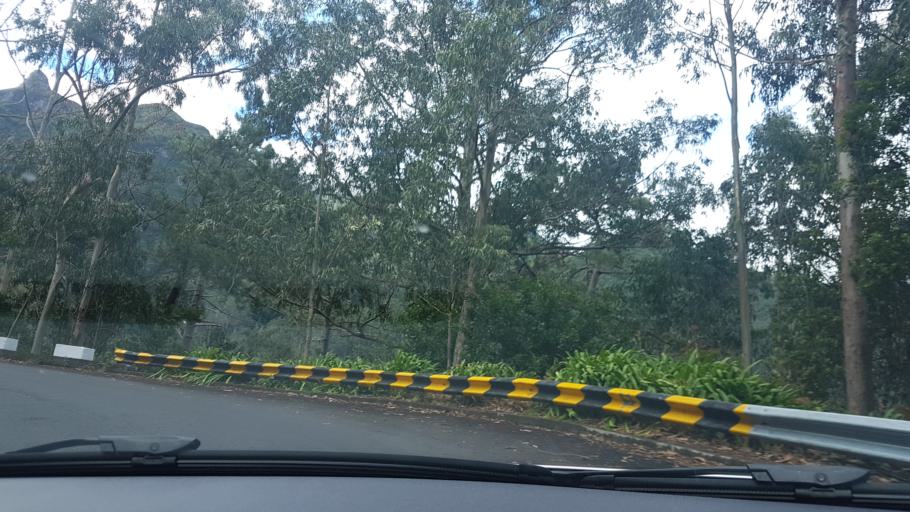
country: PT
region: Madeira
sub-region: Sao Vicente
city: Sao Vicente
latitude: 32.7662
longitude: -17.0288
